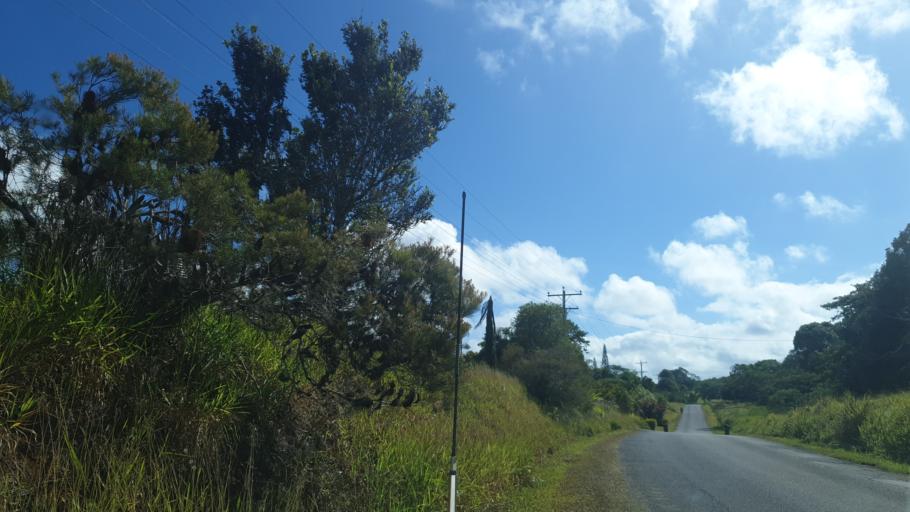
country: AU
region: Queensland
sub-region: Tablelands
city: Atherton
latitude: -17.4239
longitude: 145.6046
